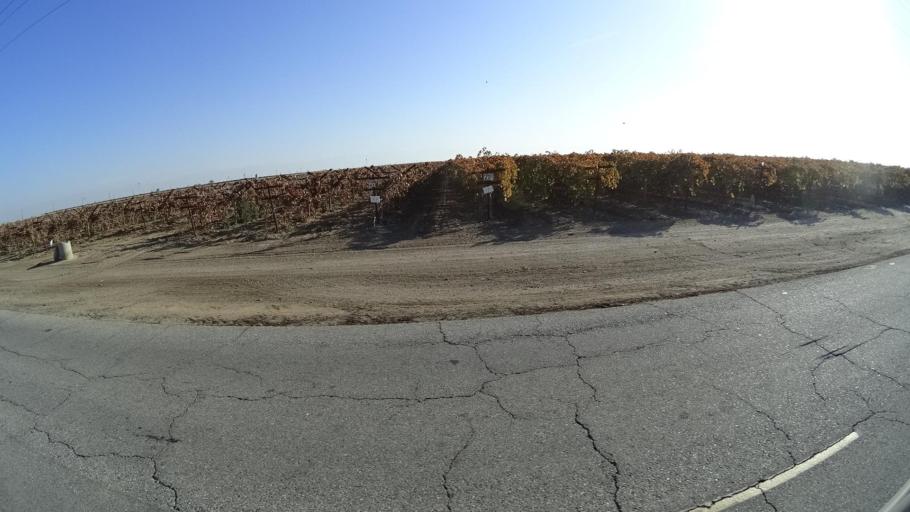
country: US
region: California
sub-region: Tulare County
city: Richgrove
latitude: 35.7706
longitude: -119.1696
